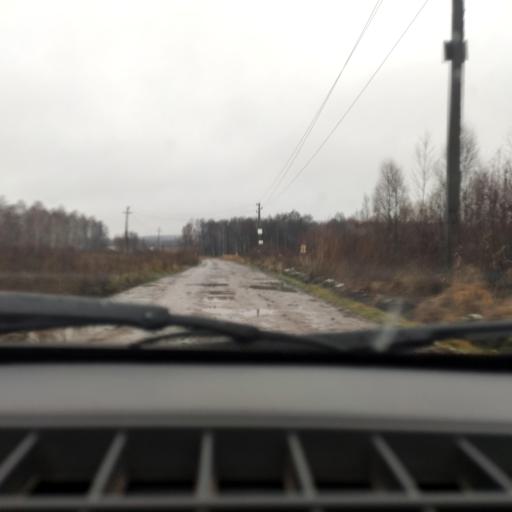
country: RU
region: Bashkortostan
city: Avdon
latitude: 54.6318
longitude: 55.7329
